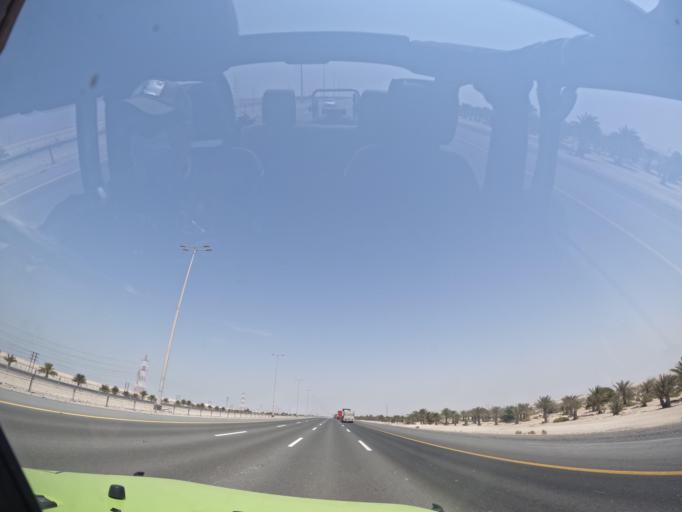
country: AE
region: Abu Dhabi
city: Abu Dhabi
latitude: 24.1980
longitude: 54.3947
